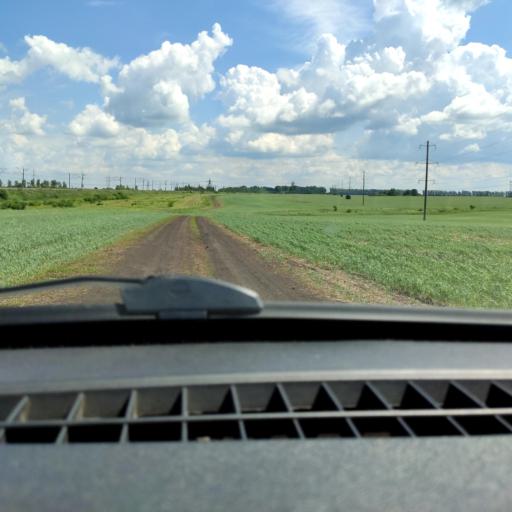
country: RU
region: Bashkortostan
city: Kabakovo
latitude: 54.5142
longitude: 56.0973
